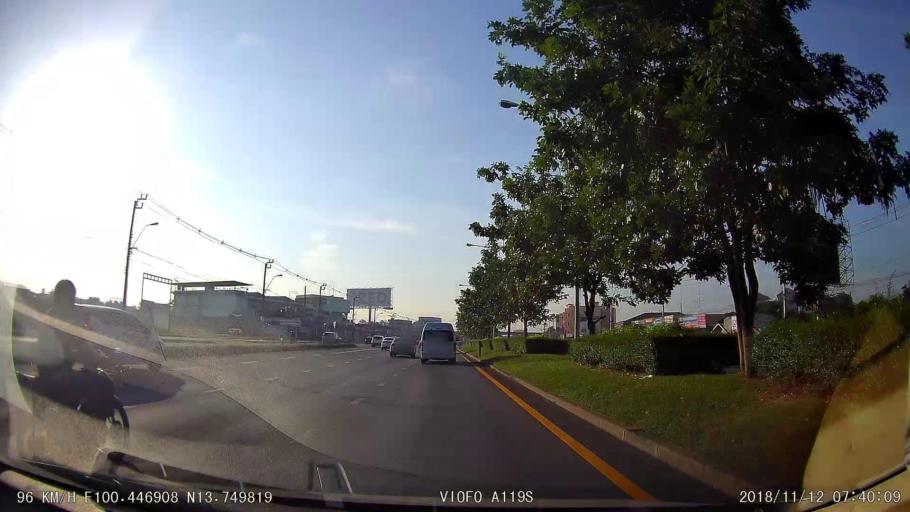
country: TH
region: Bangkok
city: Taling Chan
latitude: 13.7485
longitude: 100.4474
